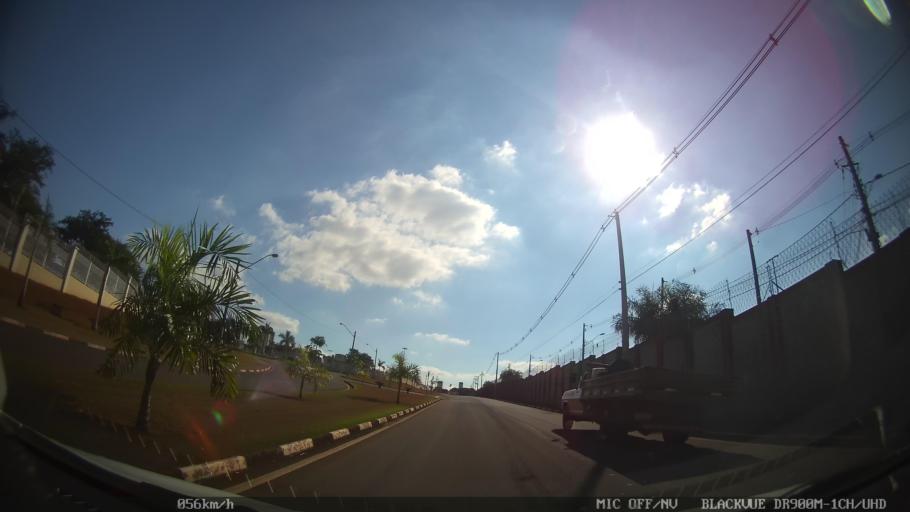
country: BR
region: Sao Paulo
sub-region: Sumare
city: Sumare
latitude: -22.8215
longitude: -47.2856
